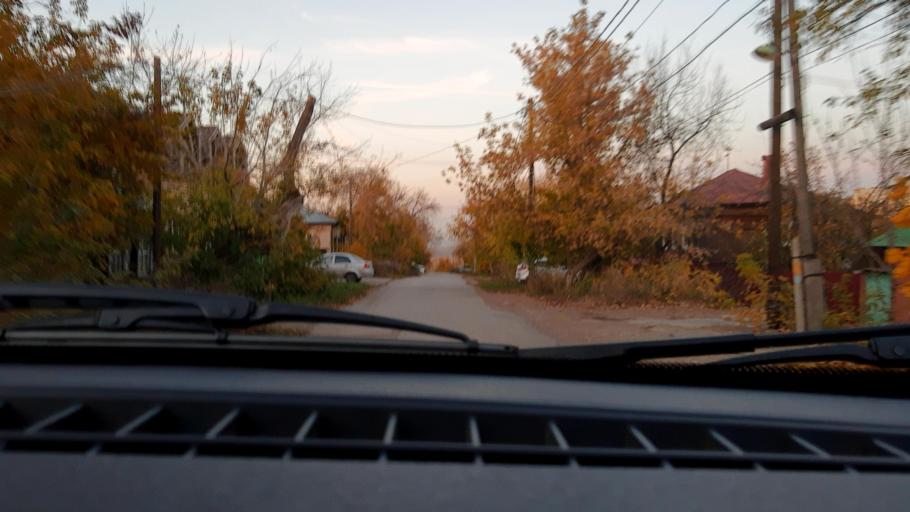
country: RU
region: Bashkortostan
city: Ufa
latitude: 54.7450
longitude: 55.9498
